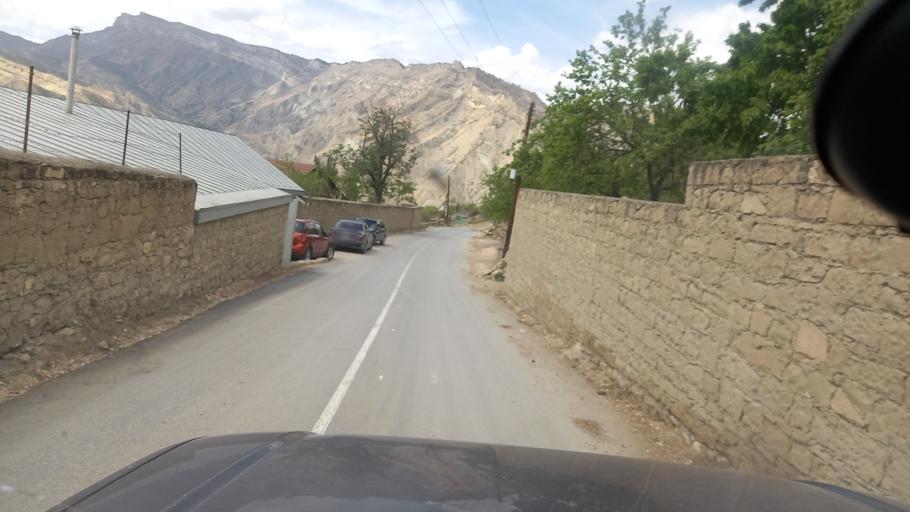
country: RU
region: Dagestan
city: Gunib
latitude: 42.3686
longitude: 46.9706
